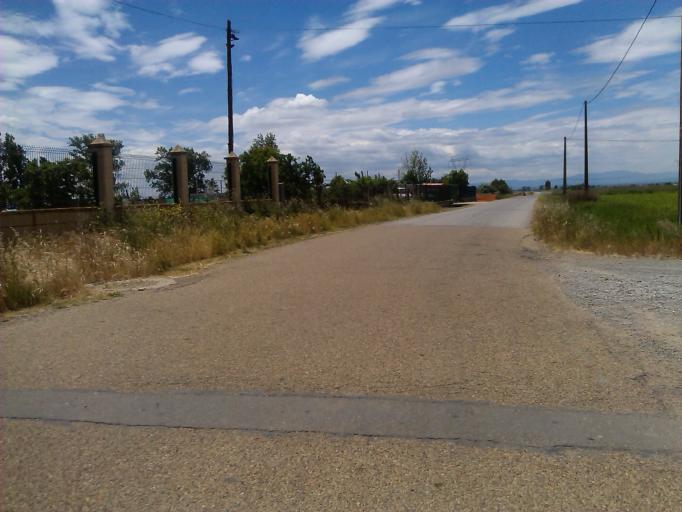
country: ES
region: Castille and Leon
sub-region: Provincia de Leon
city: Villadangos del Paramo
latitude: 42.4818
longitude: -5.7329
